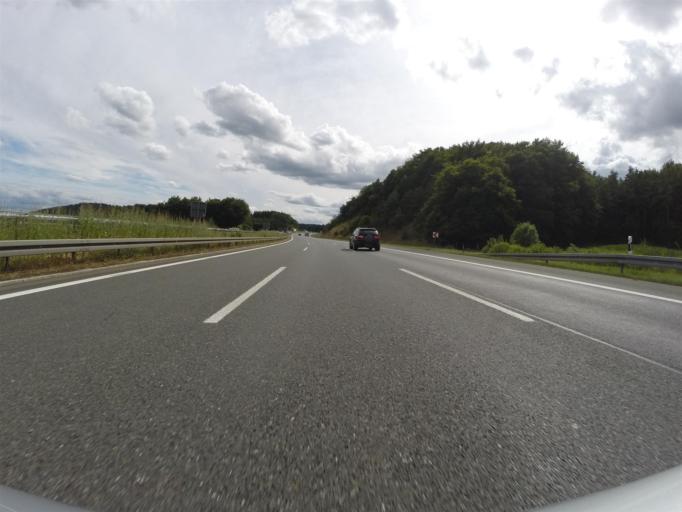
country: DE
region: Bavaria
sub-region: Upper Franconia
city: Pegnitz
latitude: 49.7732
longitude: 11.5072
